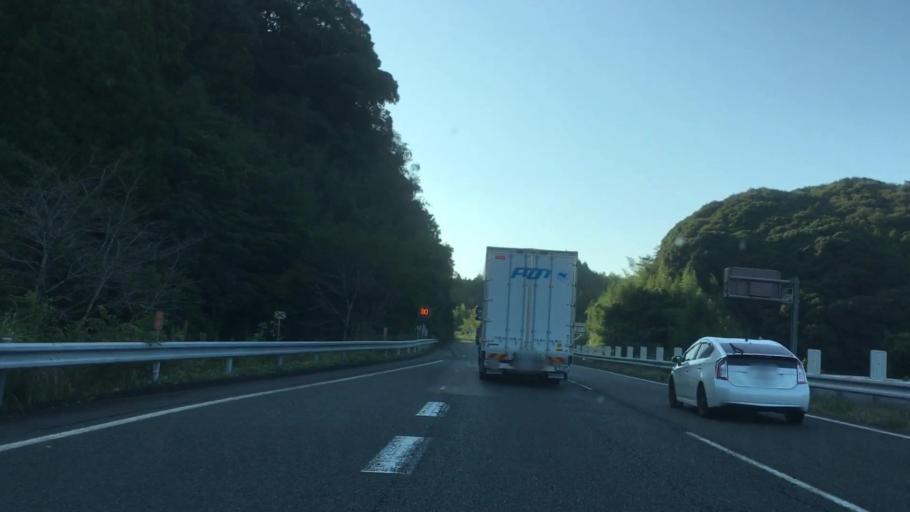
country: JP
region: Yamaguchi
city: Onoda
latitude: 34.1102
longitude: 131.1373
